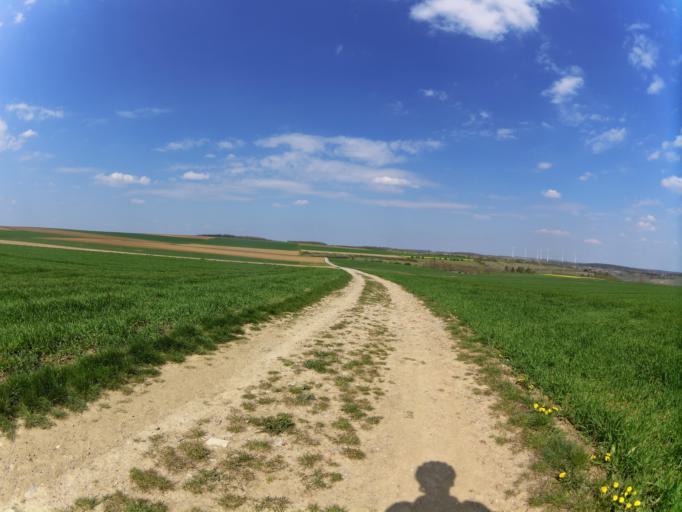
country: DE
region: Bavaria
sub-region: Regierungsbezirk Unterfranken
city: Winterhausen
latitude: 49.6822
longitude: 10.0094
